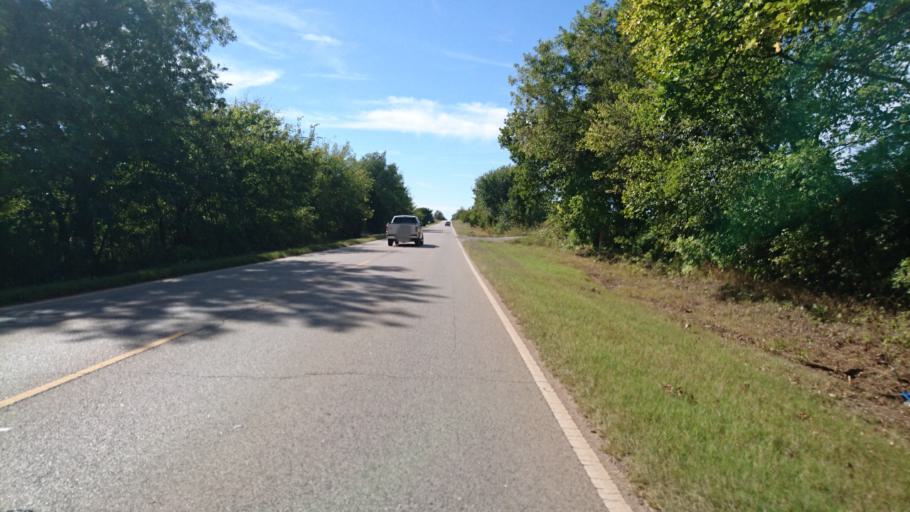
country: US
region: Oklahoma
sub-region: Lincoln County
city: Chandler
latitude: 35.7099
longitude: -96.7943
